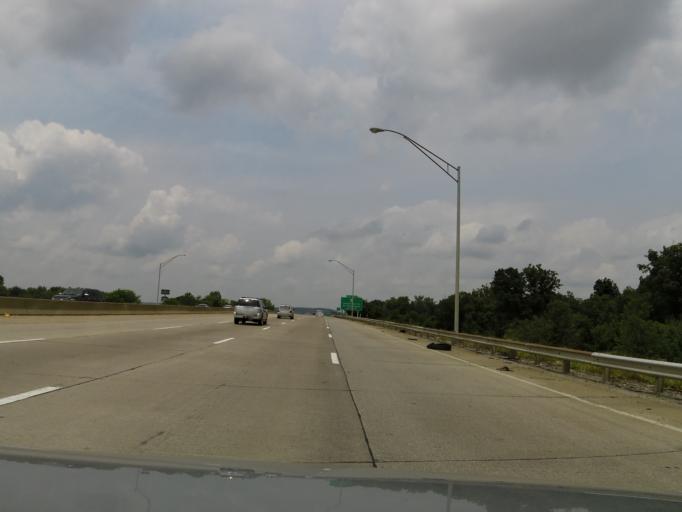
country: US
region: Kentucky
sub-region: Bullitt County
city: Shepherdsville
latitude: 37.9830
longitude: -85.6997
